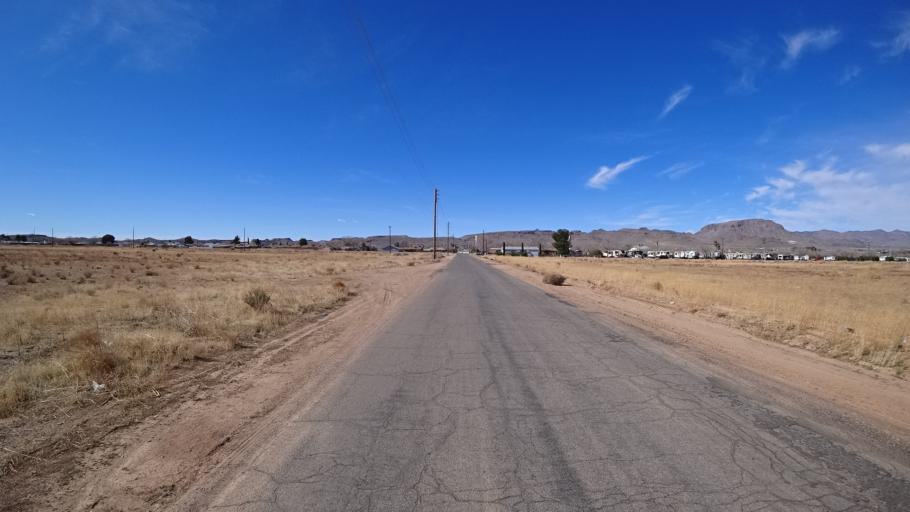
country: US
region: Arizona
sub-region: Mohave County
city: New Kingman-Butler
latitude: 35.2322
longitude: -114.0152
